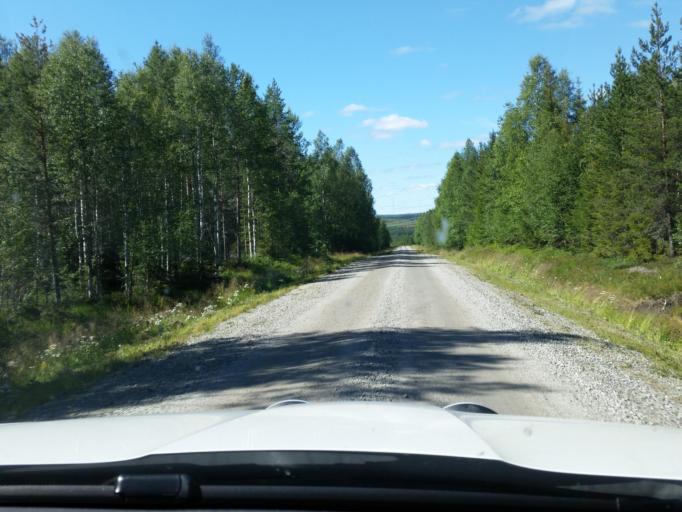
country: SE
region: Vaesterbotten
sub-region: Skelleftea Kommun
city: Storvik
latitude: 65.2150
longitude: 20.8516
